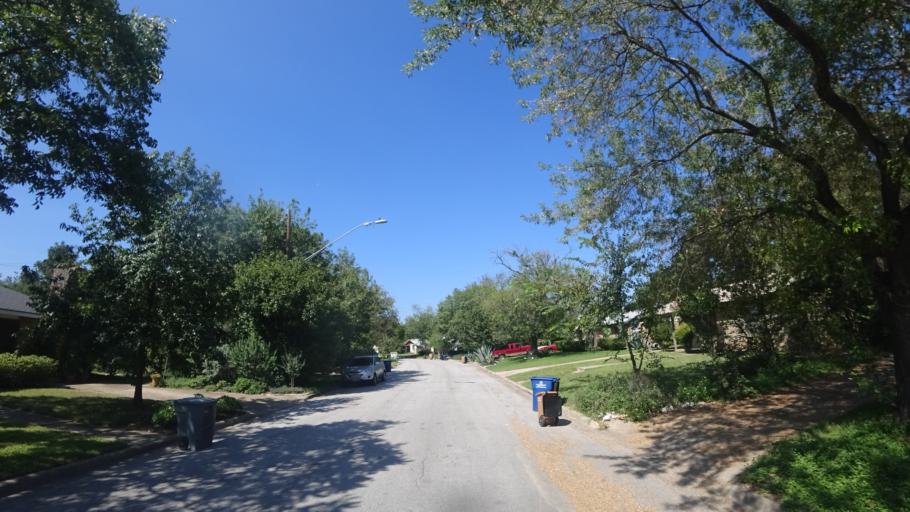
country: US
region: Texas
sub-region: Travis County
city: Austin
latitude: 30.3147
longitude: -97.6833
